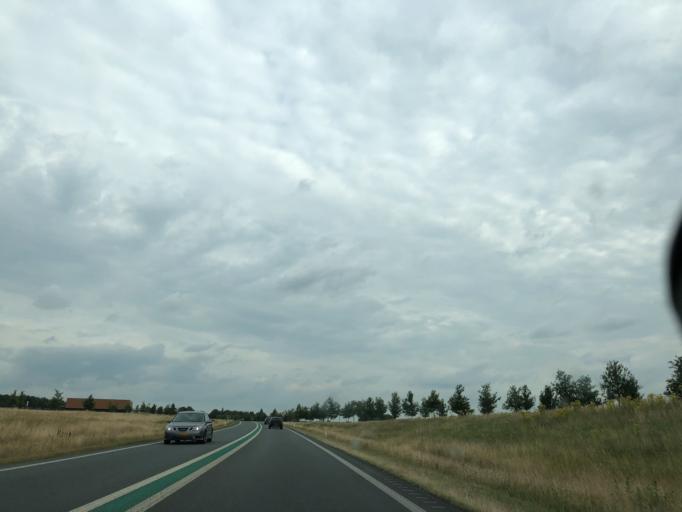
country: NL
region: Drenthe
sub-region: Gemeente Aa en Hunze
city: Anloo
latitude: 52.9978
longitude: 6.7540
